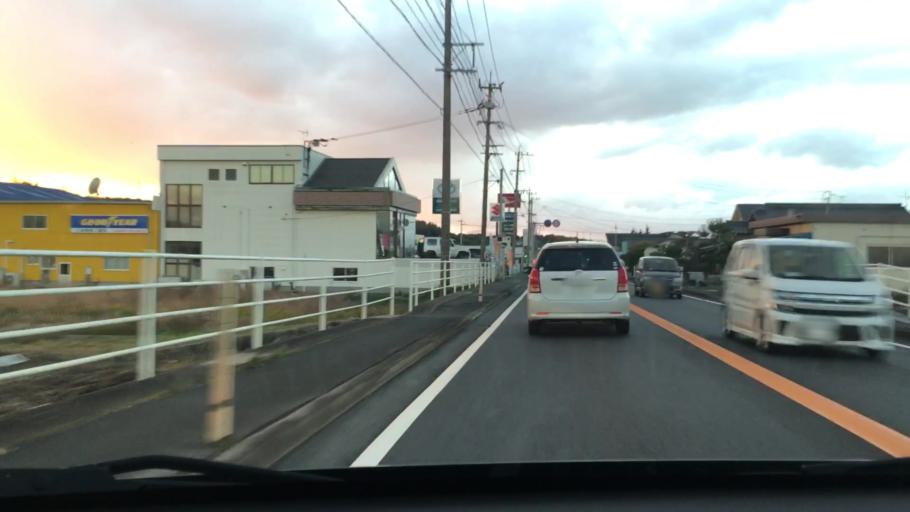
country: JP
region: Fukuoka
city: Shiida
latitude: 33.6320
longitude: 131.0812
